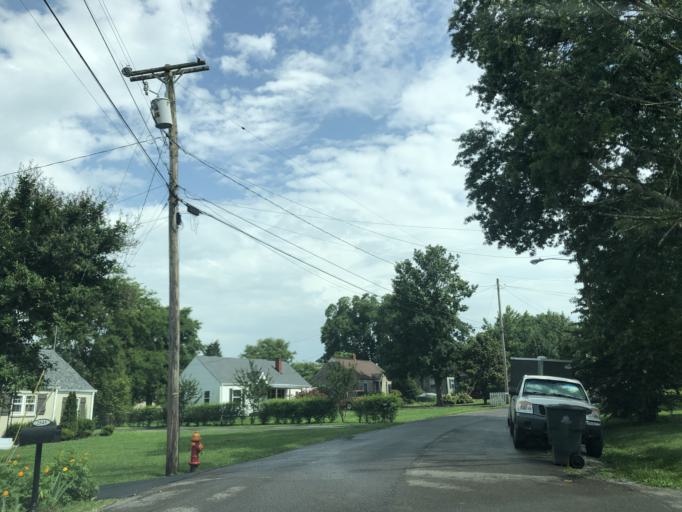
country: US
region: Tennessee
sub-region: Davidson County
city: Lakewood
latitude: 36.1739
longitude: -86.6751
